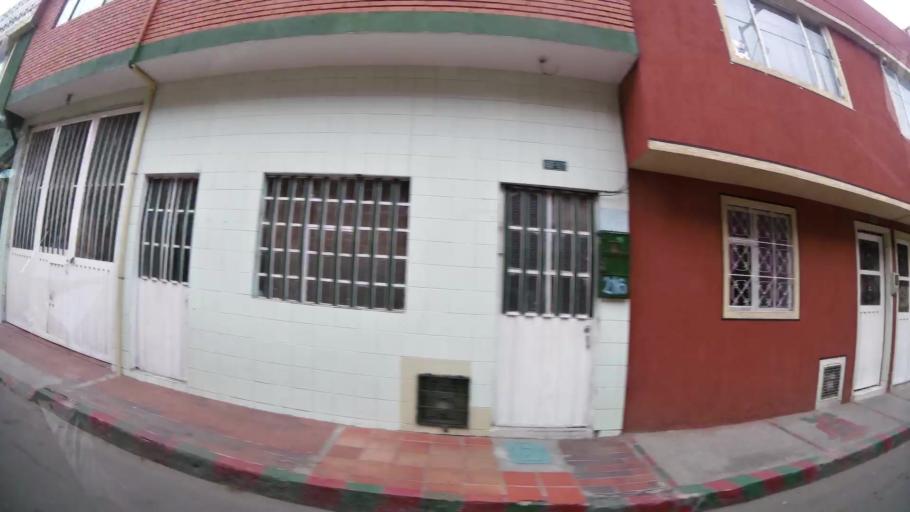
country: CO
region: Bogota D.C.
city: Bogota
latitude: 4.6042
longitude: -74.1381
